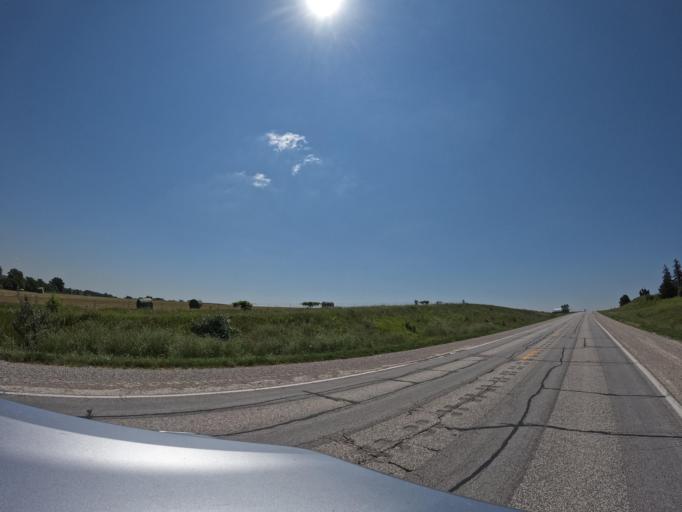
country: US
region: Iowa
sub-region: Keokuk County
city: Sigourney
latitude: 41.2789
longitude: -92.2044
